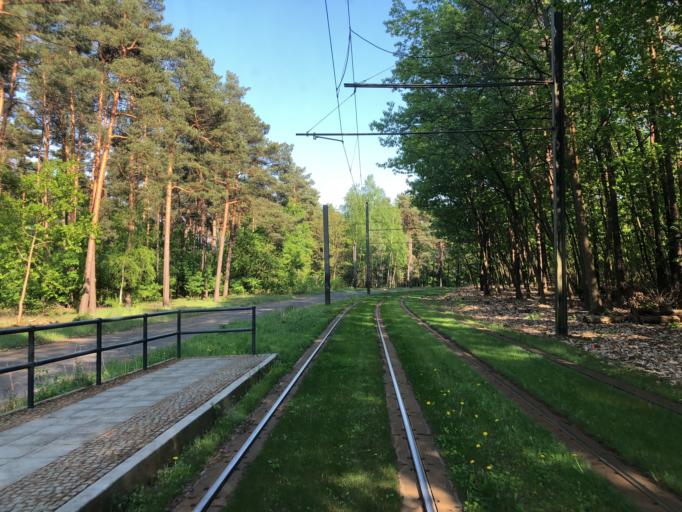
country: DE
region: Brandenburg
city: Zeuthen
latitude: 52.4058
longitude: 13.6215
